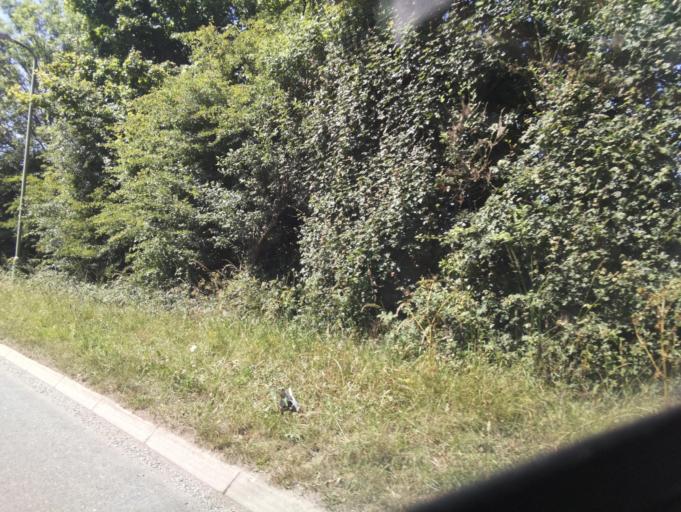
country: GB
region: England
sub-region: Devon
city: Marldon
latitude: 50.4572
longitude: -3.5877
